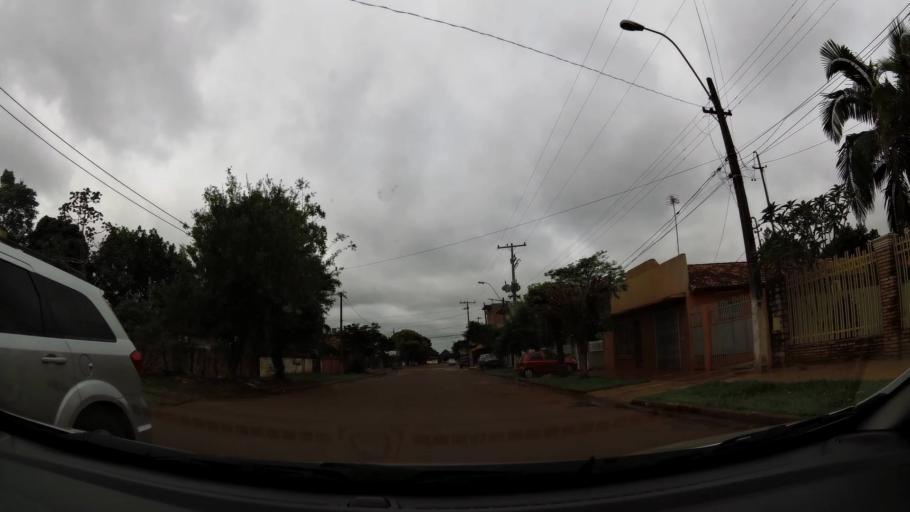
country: PY
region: Alto Parana
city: Ciudad del Este
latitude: -25.4815
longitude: -54.7610
